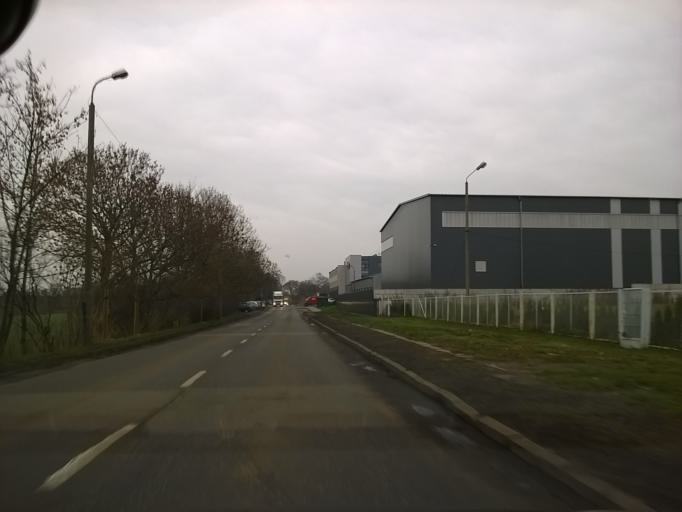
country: PL
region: Silesian Voivodeship
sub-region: Chorzow
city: Chorzow
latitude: 50.3213
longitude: 18.9822
